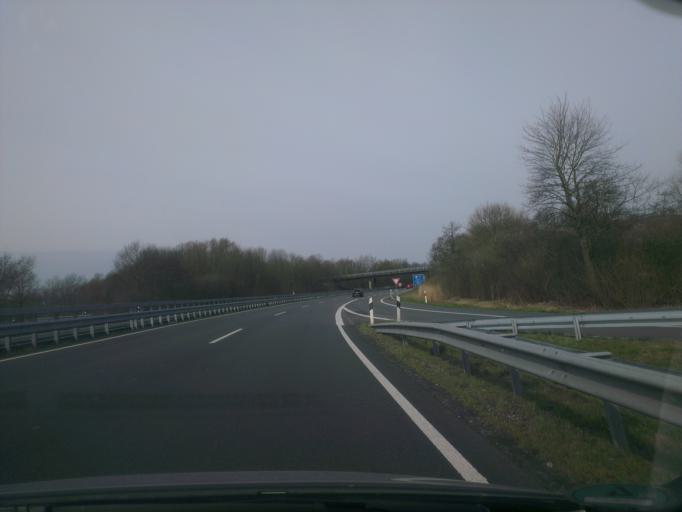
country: DE
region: Lower Saxony
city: Emden
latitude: 53.3664
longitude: 7.2451
